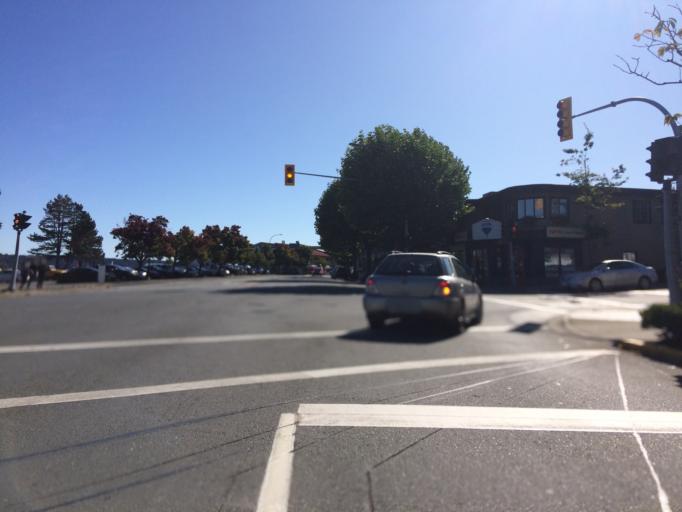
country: CA
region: British Columbia
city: Campbell River
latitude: 50.0254
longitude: -125.2420
